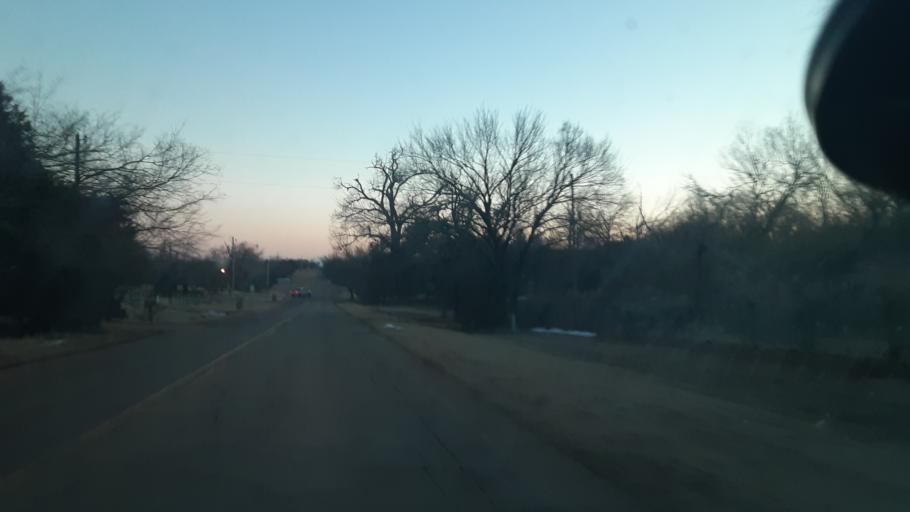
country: US
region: Oklahoma
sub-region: Oklahoma County
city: Edmond
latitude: 35.7193
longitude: -97.4252
